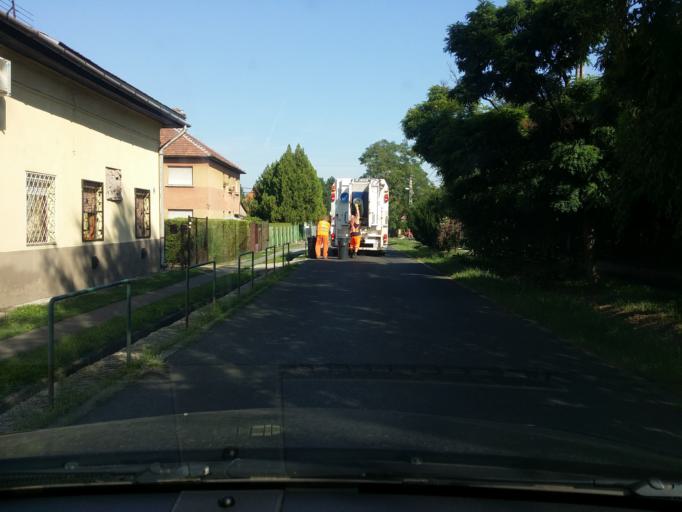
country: HU
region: Budapest
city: Budapest XVI. keruelet
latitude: 47.5270
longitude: 19.1615
